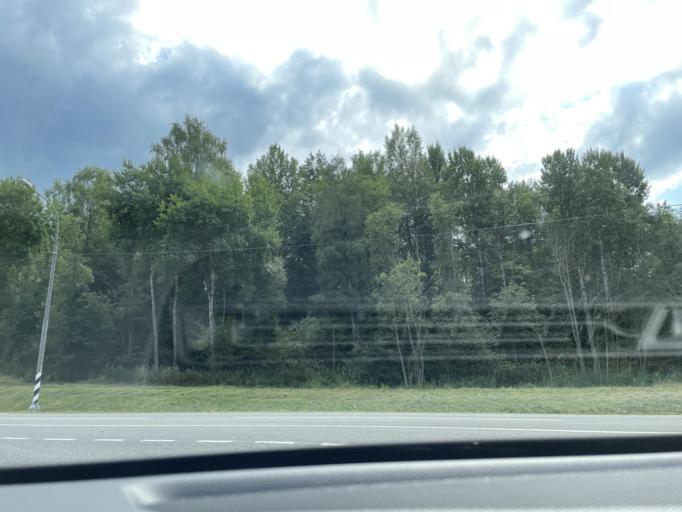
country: RU
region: Novgorod
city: Valday
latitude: 57.9981
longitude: 33.1610
